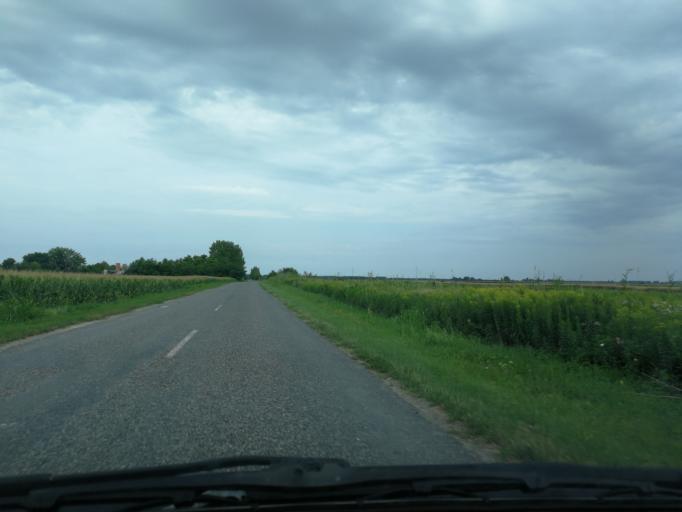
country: HU
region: Bacs-Kiskun
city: Batya
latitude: 46.4473
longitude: 18.9818
